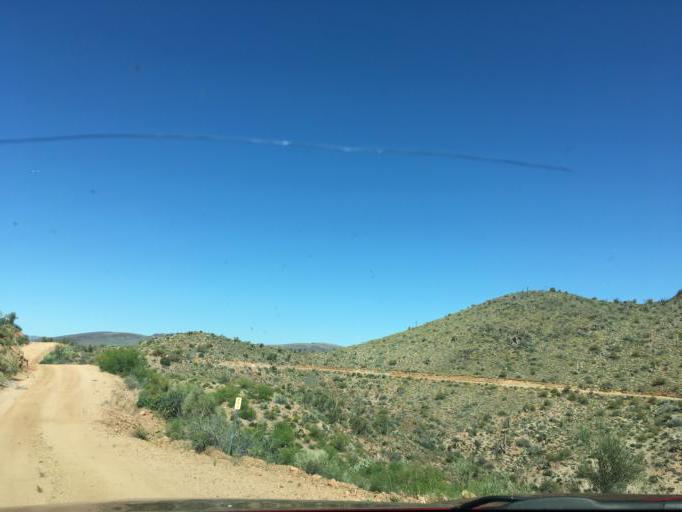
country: US
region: Arizona
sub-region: Yavapai County
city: Bagdad
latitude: 34.6096
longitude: -113.4001
